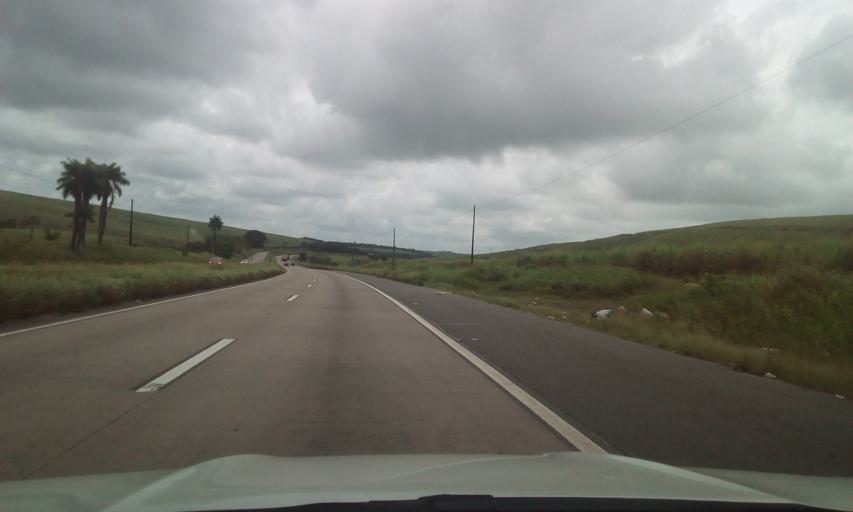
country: BR
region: Pernambuco
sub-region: Itapissuma
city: Itapissuma
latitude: -7.7803
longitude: -34.9319
